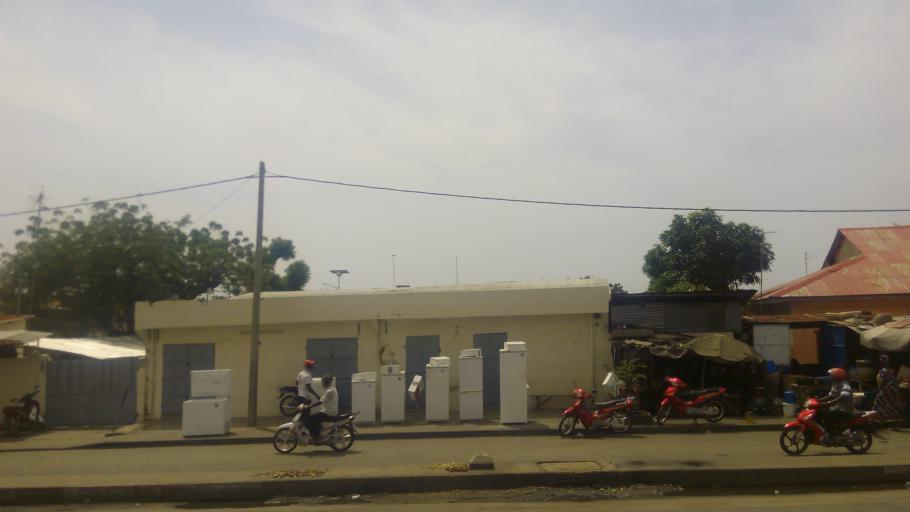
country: BJ
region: Littoral
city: Cotonou
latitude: 6.3582
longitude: 2.4252
